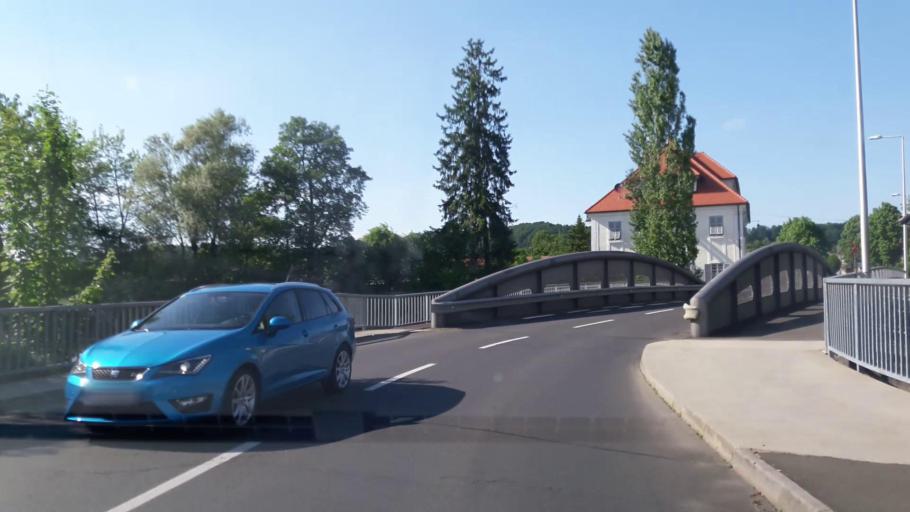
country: AT
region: Styria
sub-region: Politischer Bezirk Suedoststeiermark
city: Fehring
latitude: 46.9448
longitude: 16.0090
